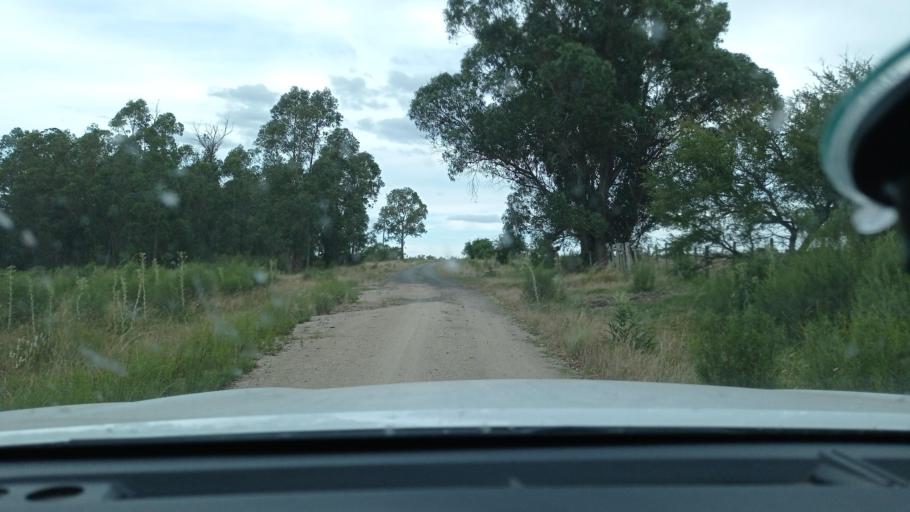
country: UY
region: Florida
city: Casupa
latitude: -34.1446
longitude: -55.7968
